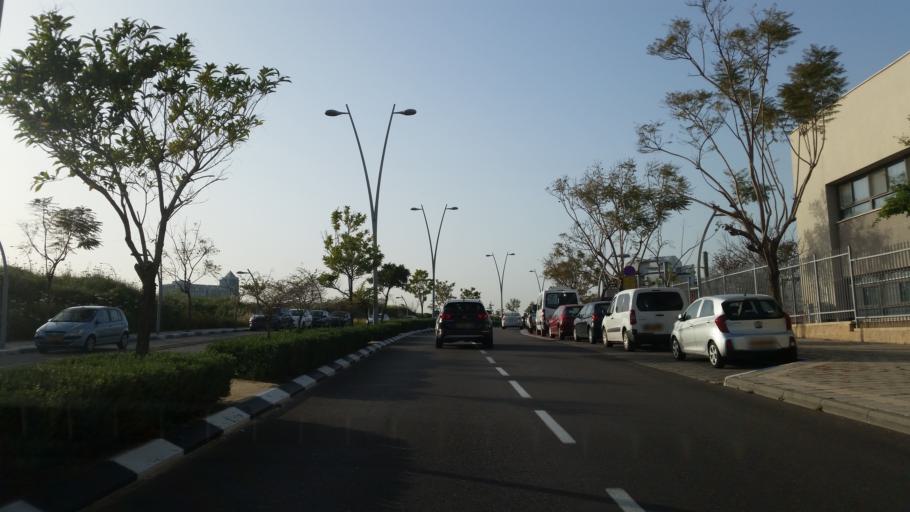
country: IL
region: Central District
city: Ra'anana
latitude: 32.1927
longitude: 34.8904
